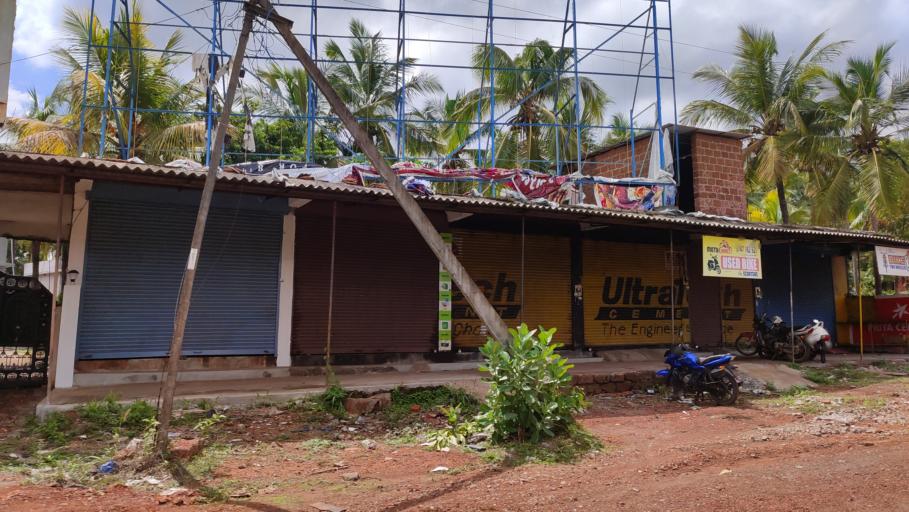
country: IN
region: Kerala
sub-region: Kasaragod District
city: Kannangad
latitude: 12.3868
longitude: 75.1007
